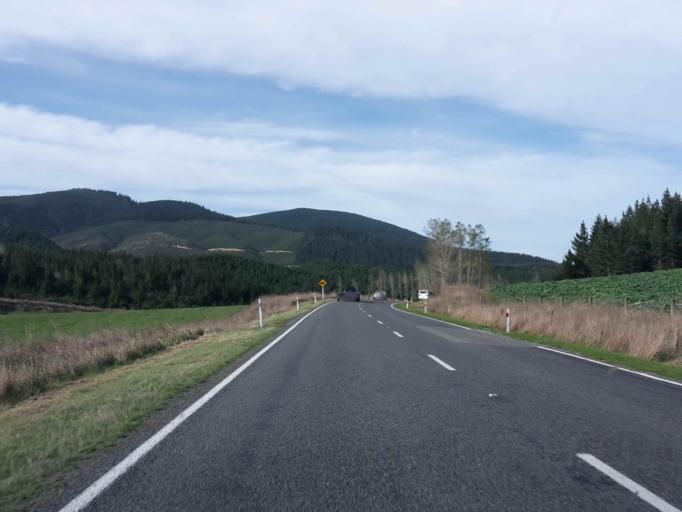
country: NZ
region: Canterbury
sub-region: Timaru District
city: Pleasant Point
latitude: -44.1202
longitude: 171.0540
